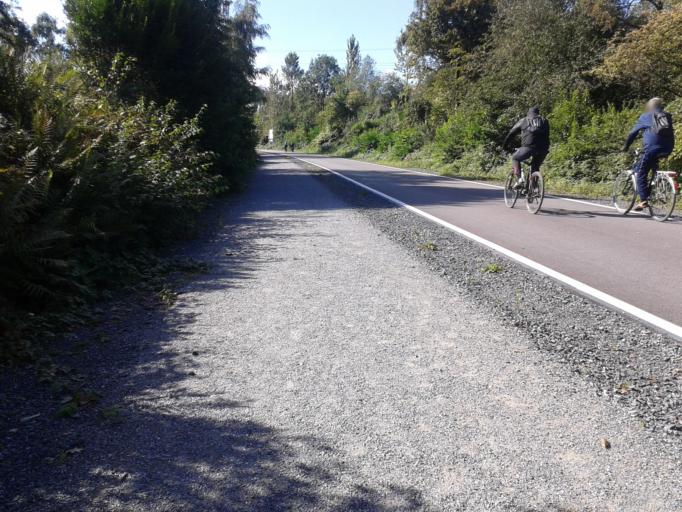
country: DE
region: North Rhine-Westphalia
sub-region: Regierungsbezirk Dusseldorf
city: Muelheim (Ruhr)
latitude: 51.4482
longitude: 6.9472
